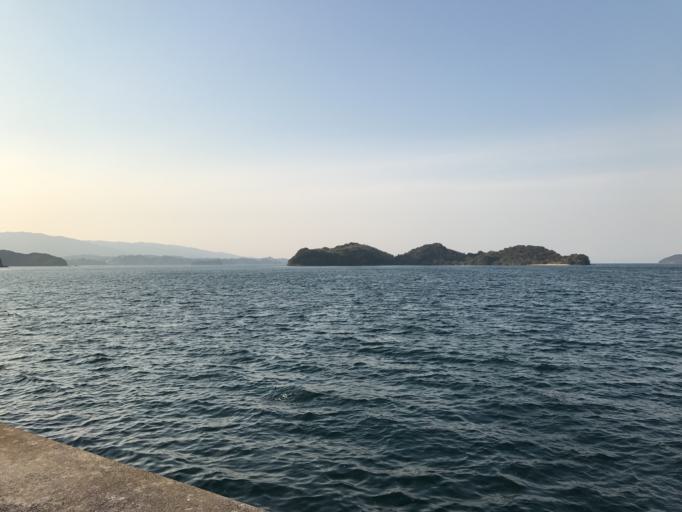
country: JP
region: Nagasaki
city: Togitsu
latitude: 32.8561
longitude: 129.8258
